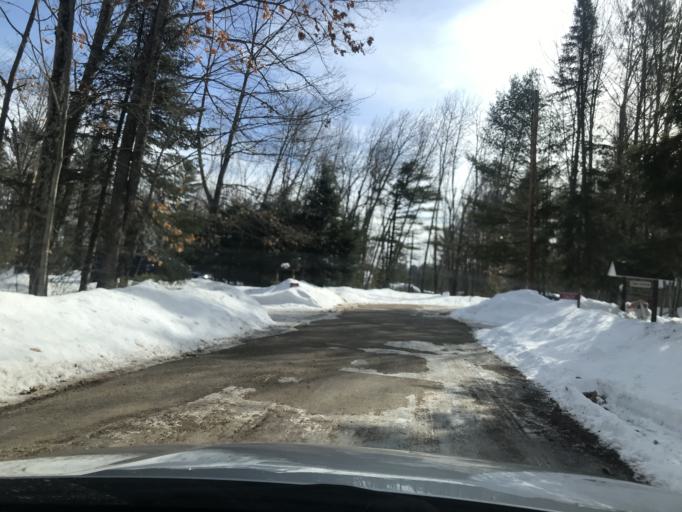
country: US
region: Wisconsin
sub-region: Menominee County
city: Legend Lake
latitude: 45.1193
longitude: -88.4422
